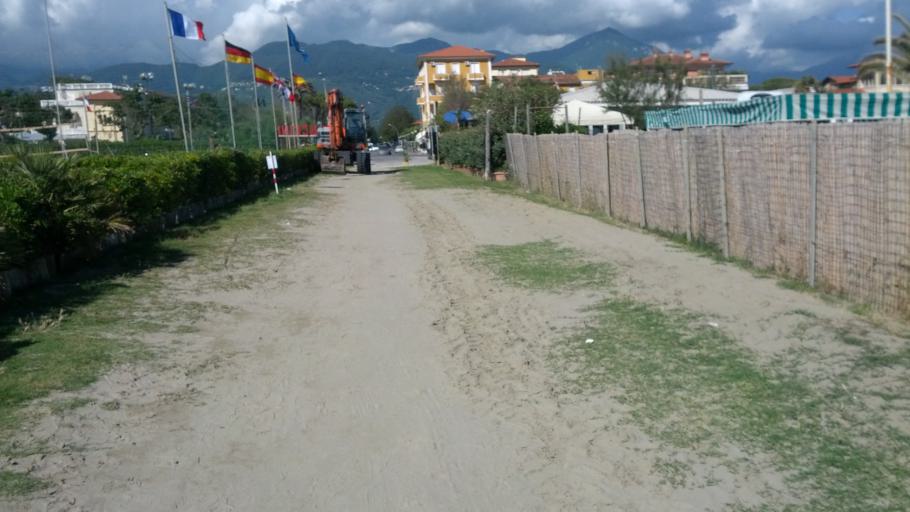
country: IT
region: Tuscany
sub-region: Provincia di Lucca
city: Pietrasanta
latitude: 43.9362
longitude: 10.1891
